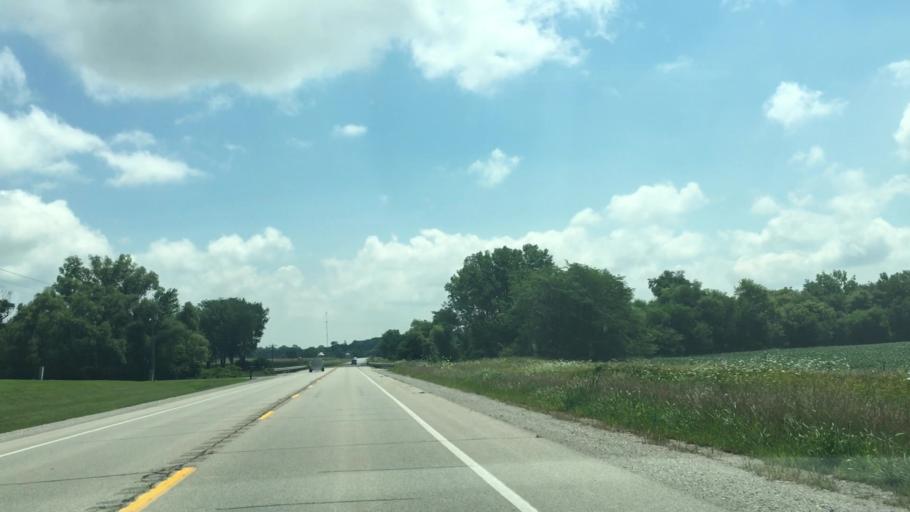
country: US
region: Iowa
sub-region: Johnson County
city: Tiffin
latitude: 41.7145
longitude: -91.7132
